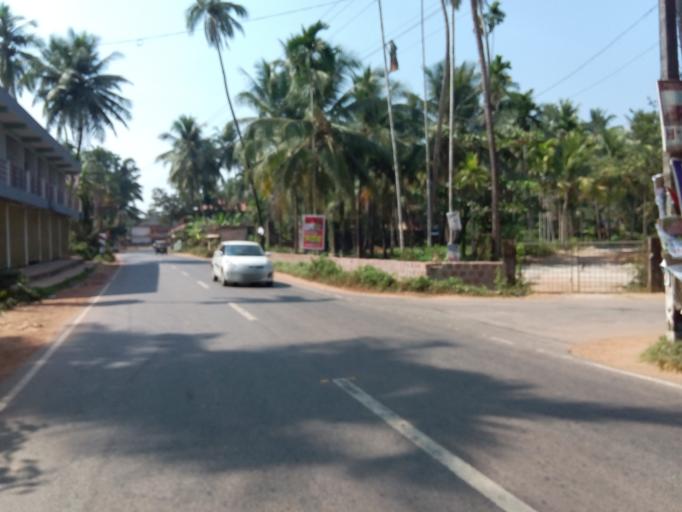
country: IN
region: Kerala
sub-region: Kozhikode
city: Nadapuram
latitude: 11.6876
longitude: 75.6728
